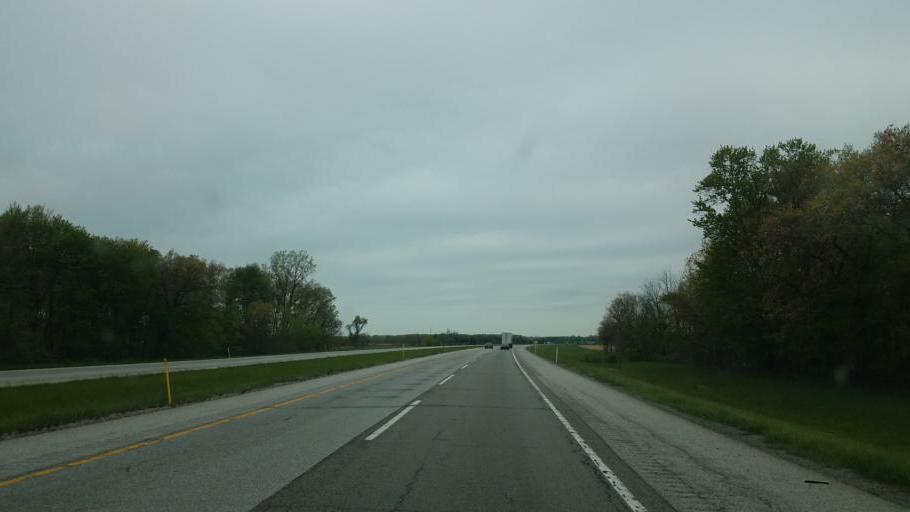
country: US
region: Michigan
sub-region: Saint Joseph County
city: White Pigeon
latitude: 41.7516
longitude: -85.6233
